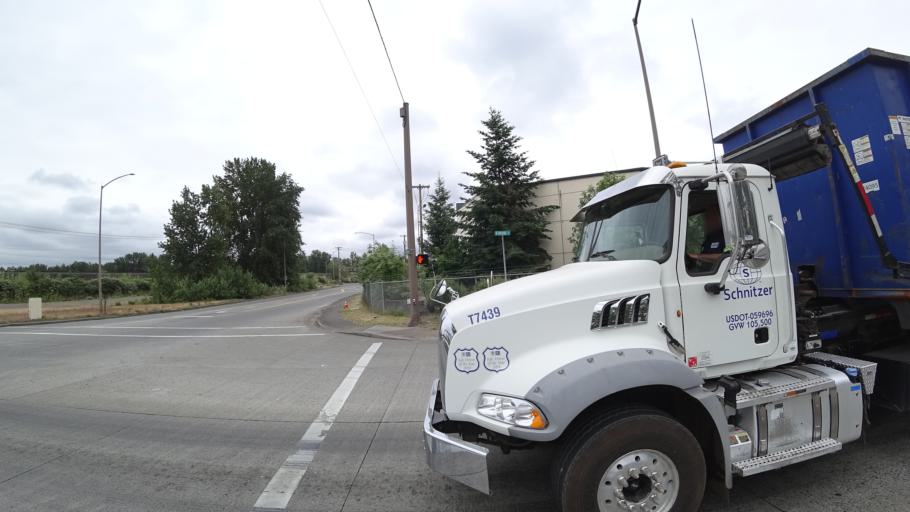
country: US
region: Washington
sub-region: Clark County
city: Vancouver
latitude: 45.6138
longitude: -122.7045
